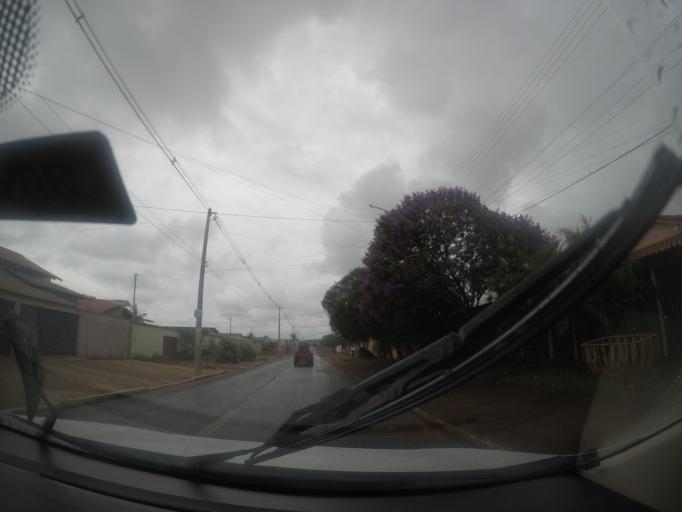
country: BR
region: Goias
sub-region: Trindade
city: Trindade
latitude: -16.6399
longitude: -49.3879
